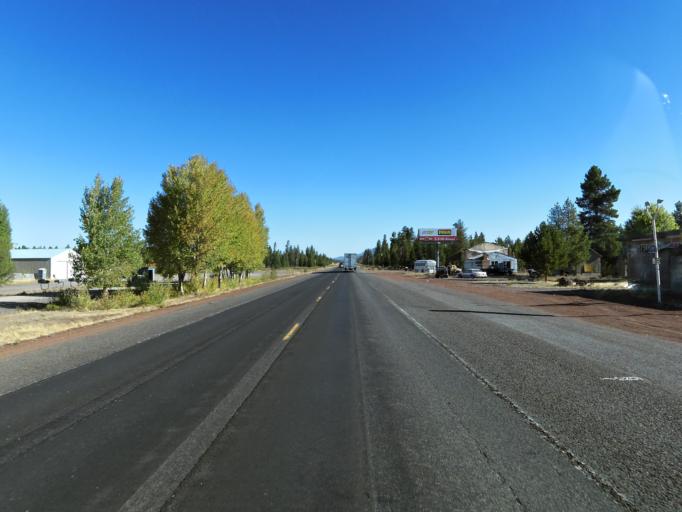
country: US
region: Oregon
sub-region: Deschutes County
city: La Pine
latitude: 43.1337
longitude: -121.8032
